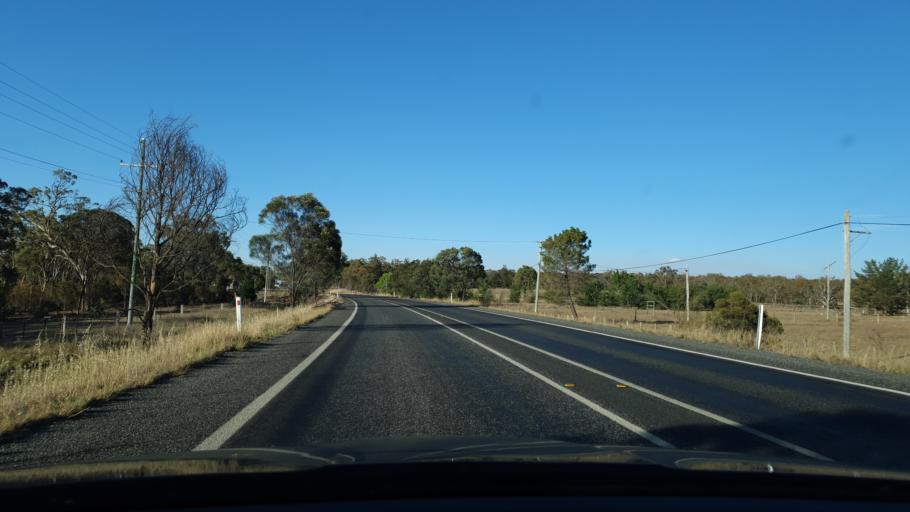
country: AU
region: Queensland
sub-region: Southern Downs
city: Stanthorpe
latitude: -28.7015
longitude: 151.9048
